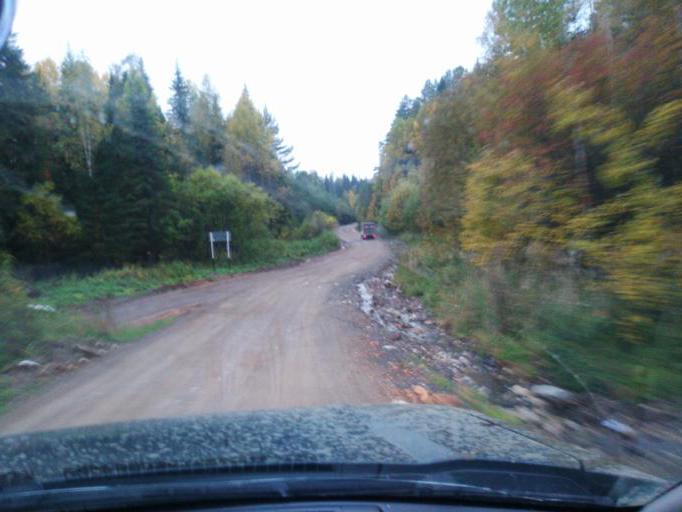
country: RU
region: Sverdlovsk
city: Sylva
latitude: 57.8131
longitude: 58.6046
